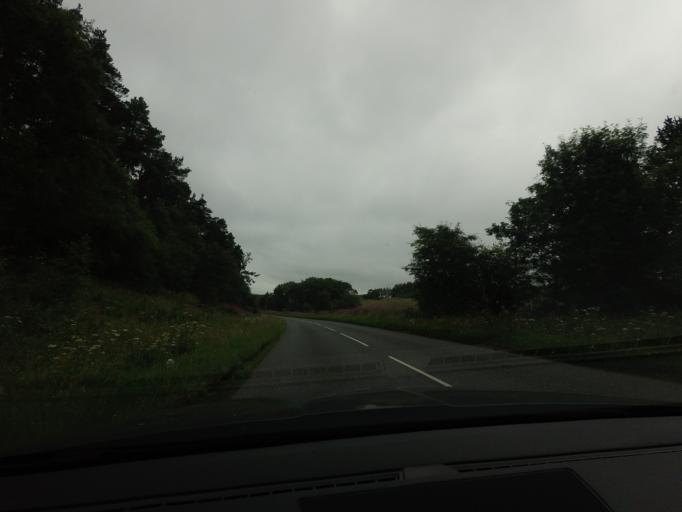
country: GB
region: Scotland
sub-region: Highland
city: Alness
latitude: 58.0099
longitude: -4.3954
